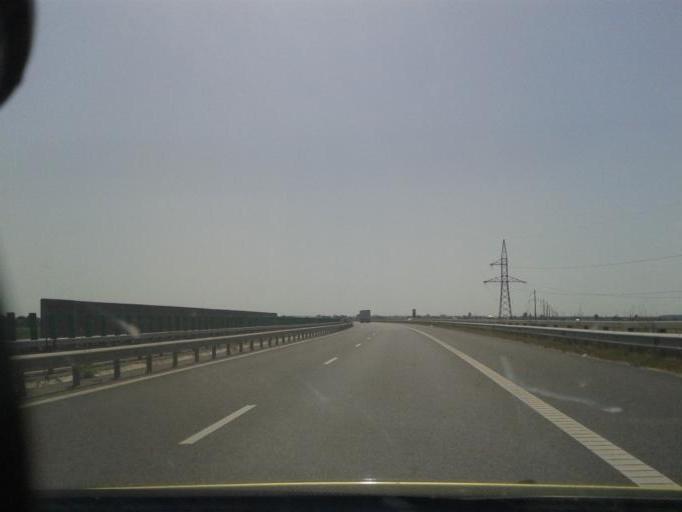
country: RO
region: Prahova
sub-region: Comuna Barcanesti
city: Barcanesti
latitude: 44.8807
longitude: 26.0360
